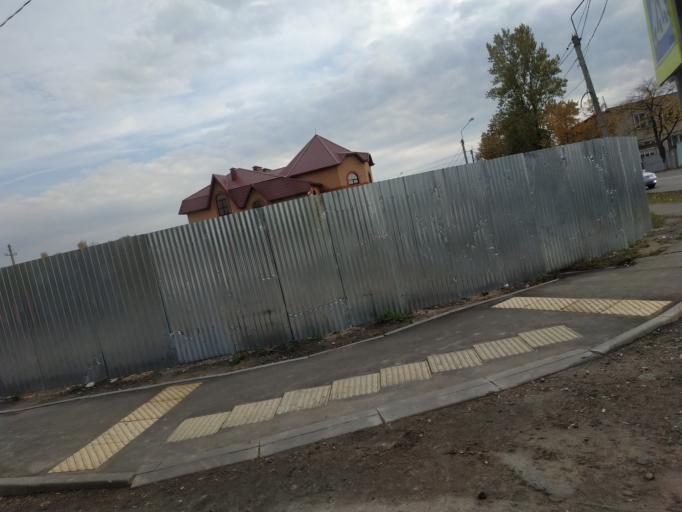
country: RU
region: Moskovskaya
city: Mozhaysk
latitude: 55.4989
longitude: 36.0176
